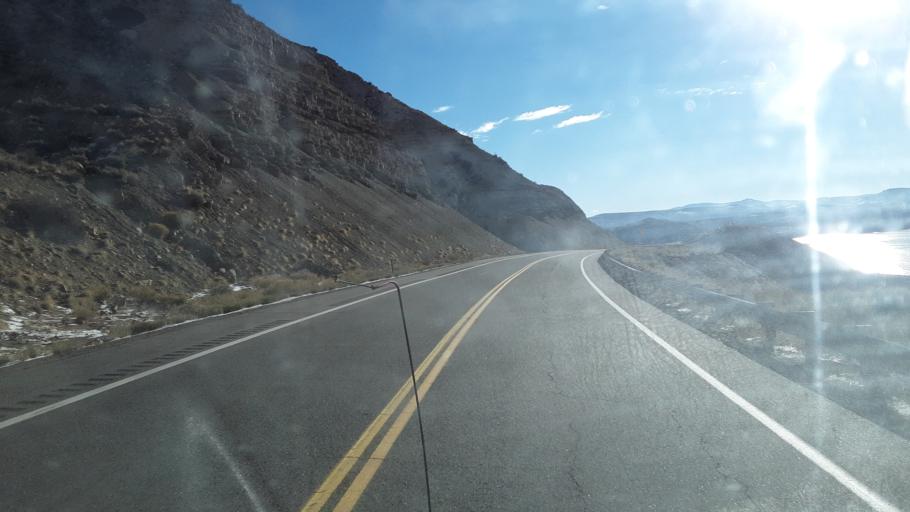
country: US
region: Colorado
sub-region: Gunnison County
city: Gunnison
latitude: 38.4831
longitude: -107.1983
